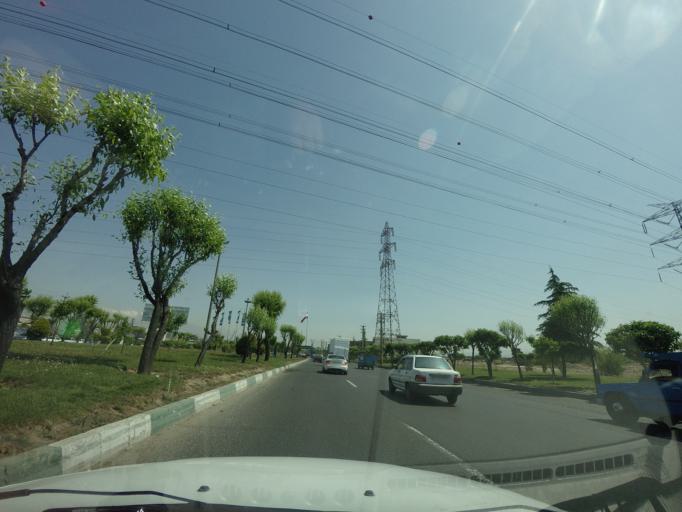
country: IR
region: Tehran
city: Eslamshahr
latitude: 35.6153
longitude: 51.3150
